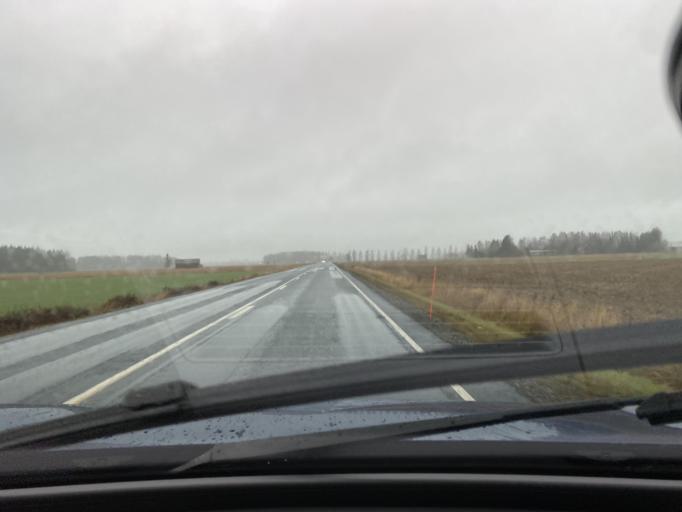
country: FI
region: Varsinais-Suomi
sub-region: Loimaa
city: Alastaro
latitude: 60.8925
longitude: 22.9642
